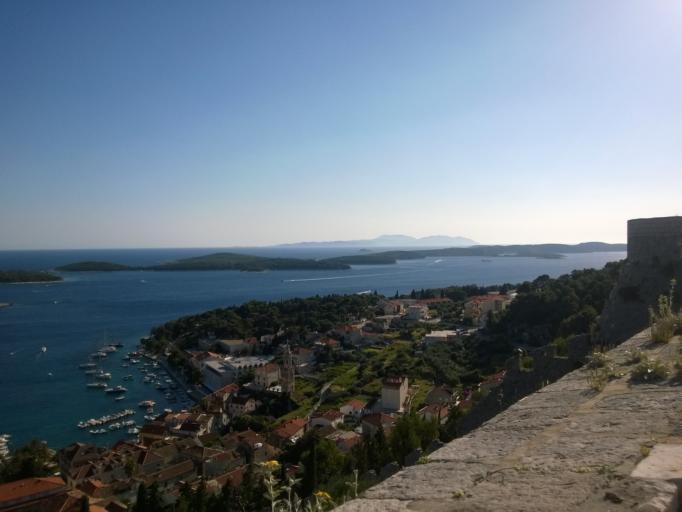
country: HR
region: Splitsko-Dalmatinska
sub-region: Grad Hvar
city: Hvar
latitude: 43.1746
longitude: 16.4422
